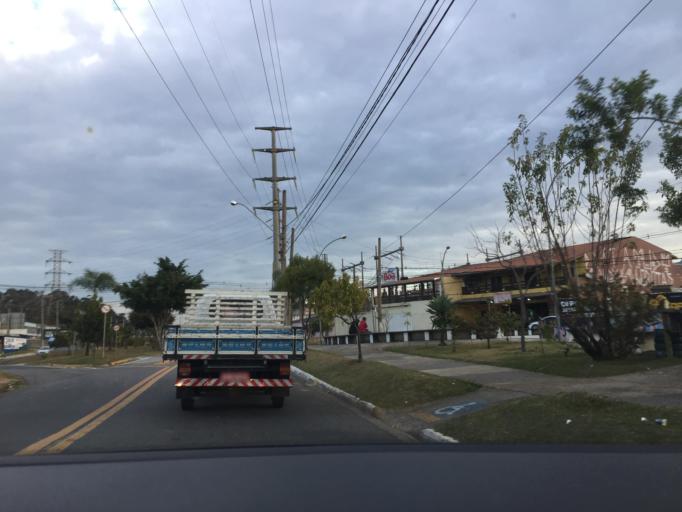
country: BR
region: Sao Paulo
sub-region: Varzea Paulista
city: Varzea Paulista
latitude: -23.2114
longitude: -46.8397
